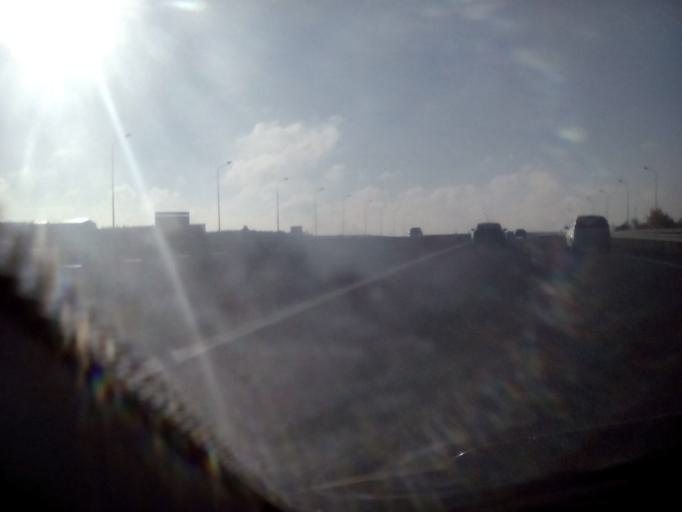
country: PL
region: Masovian Voivodeship
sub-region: Powiat grojecki
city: Grojec
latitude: 51.8326
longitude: 20.8779
